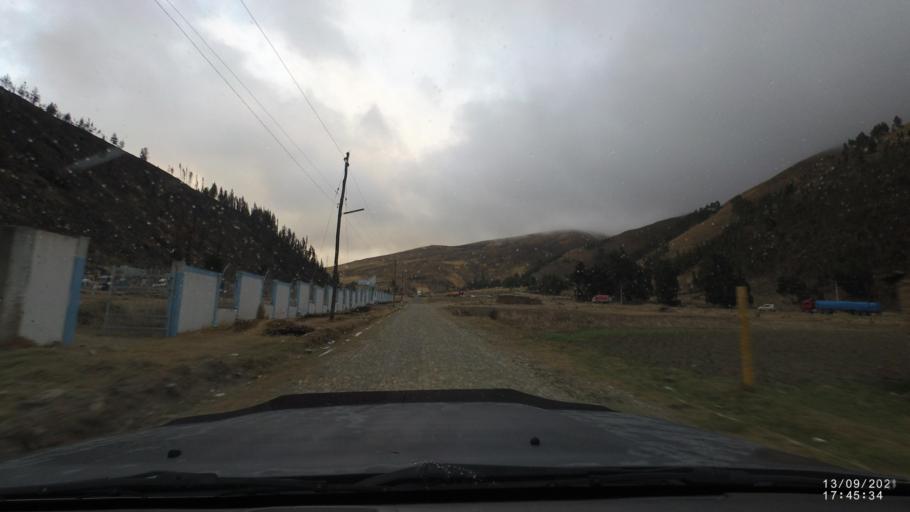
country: BO
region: Cochabamba
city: Colomi
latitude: -17.3784
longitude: -65.8331
